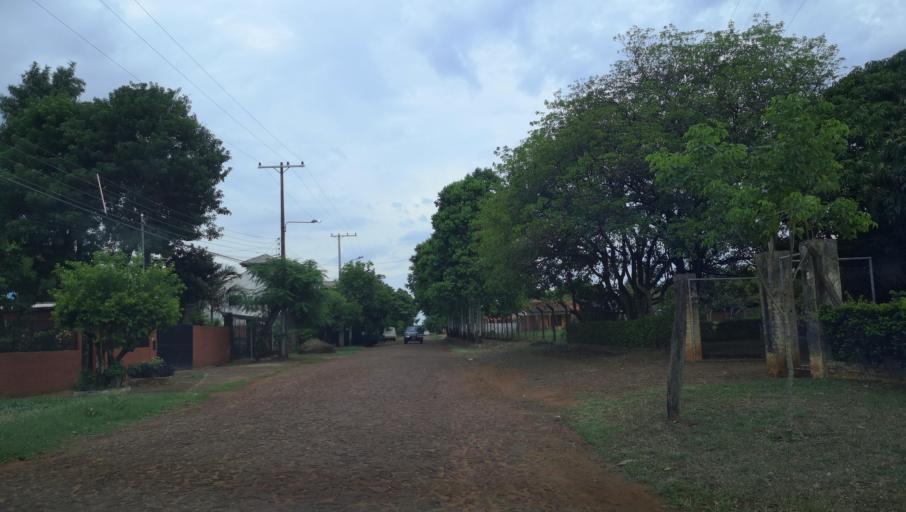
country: PY
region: Misiones
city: Santa Maria
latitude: -26.8856
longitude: -57.0429
